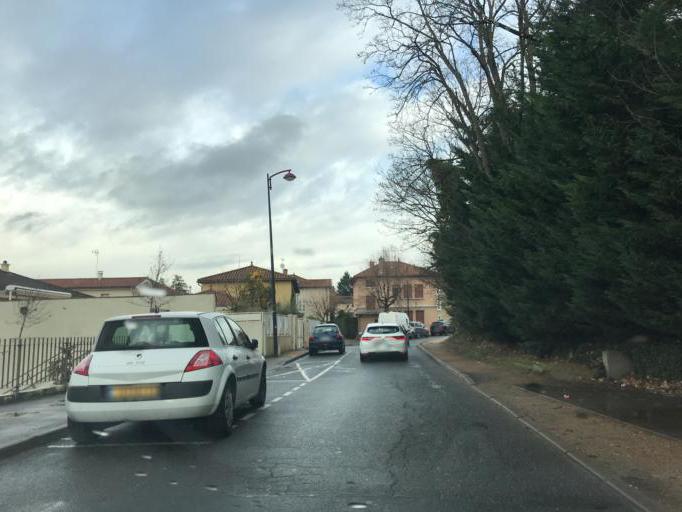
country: FR
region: Rhone-Alpes
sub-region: Departement de l'Ain
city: Jassans-Riottier
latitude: 45.9851
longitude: 4.7579
